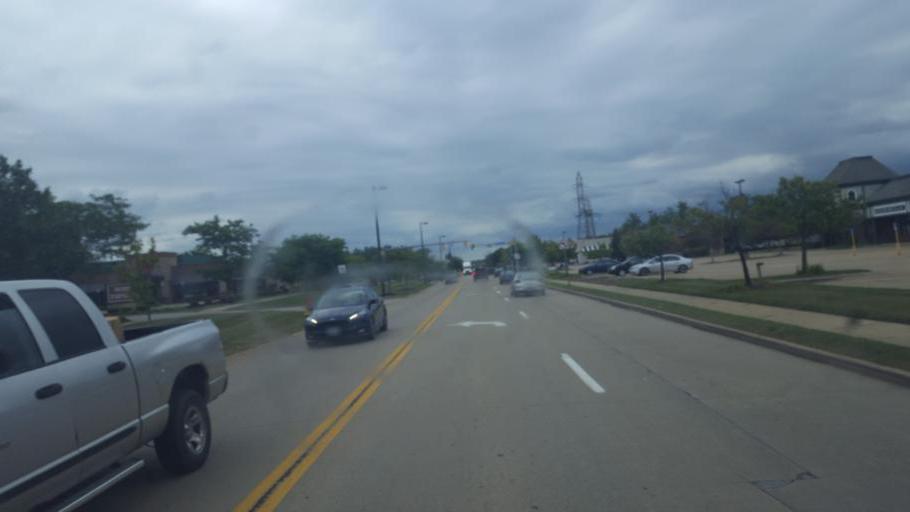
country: US
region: Ohio
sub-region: Lake County
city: Fairport Harbor
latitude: 41.7148
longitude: -81.2994
